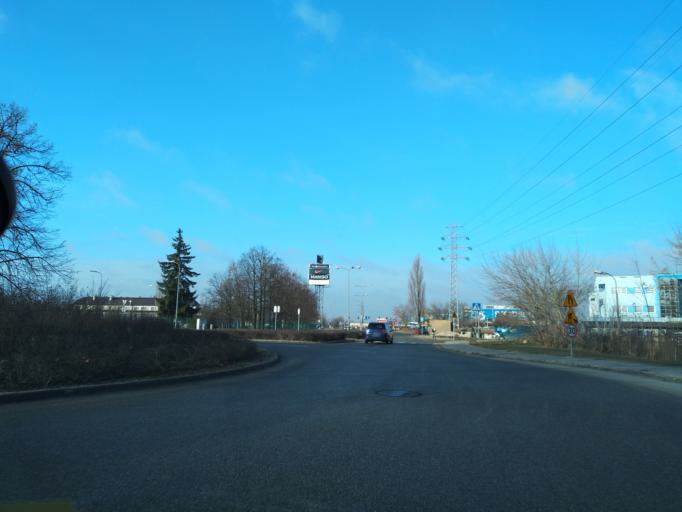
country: PL
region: Masovian Voivodeship
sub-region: Powiat piaseczynski
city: Piaseczno
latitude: 52.0890
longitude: 21.0233
